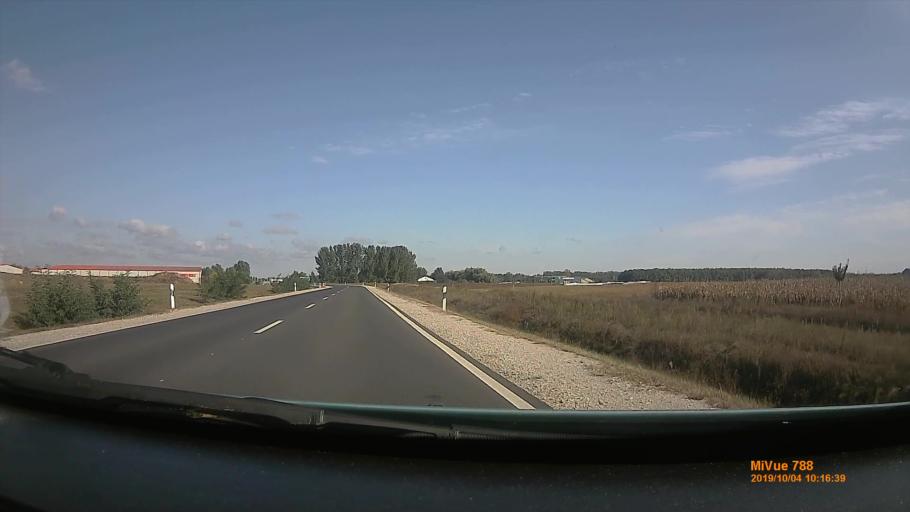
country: HU
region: Szabolcs-Szatmar-Bereg
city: Nyiregyhaza
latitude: 47.9513
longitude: 21.6545
